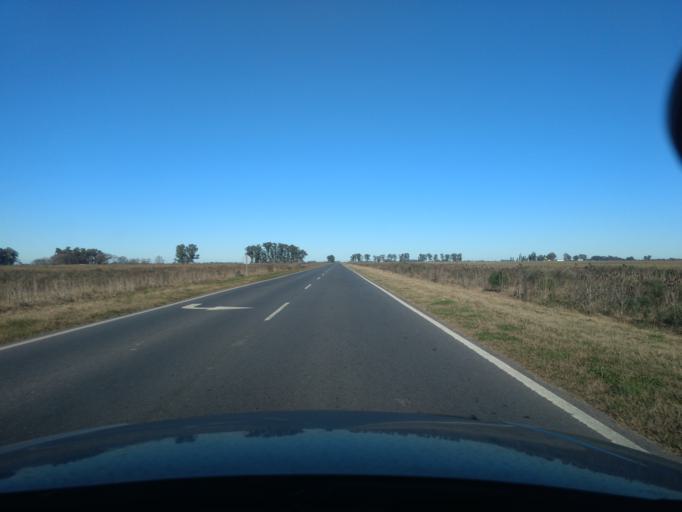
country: AR
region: Buenos Aires
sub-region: Partido de Navarro
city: Navarro
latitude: -34.8342
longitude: -59.1990
